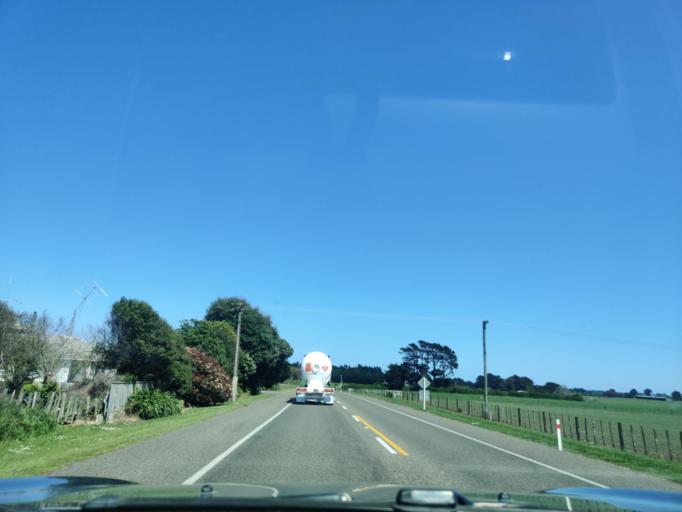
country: NZ
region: Manawatu-Wanganui
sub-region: Wanganui District
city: Wanganui
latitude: -39.8223
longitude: 174.8528
